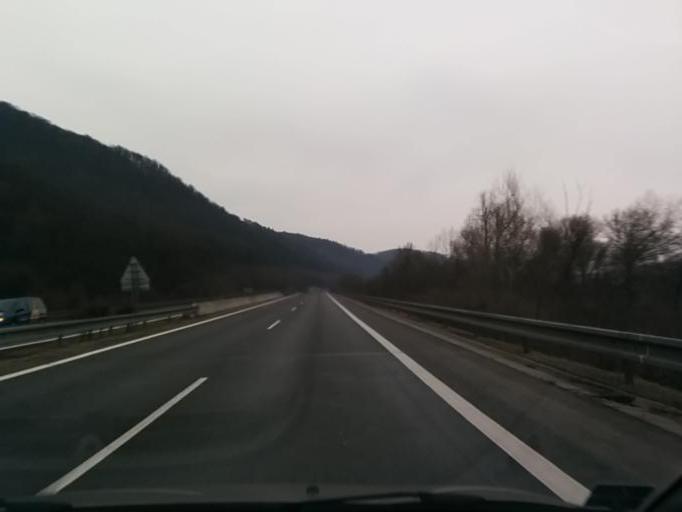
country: SK
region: Banskobystricky
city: Nova Bana
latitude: 48.4228
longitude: 18.6672
